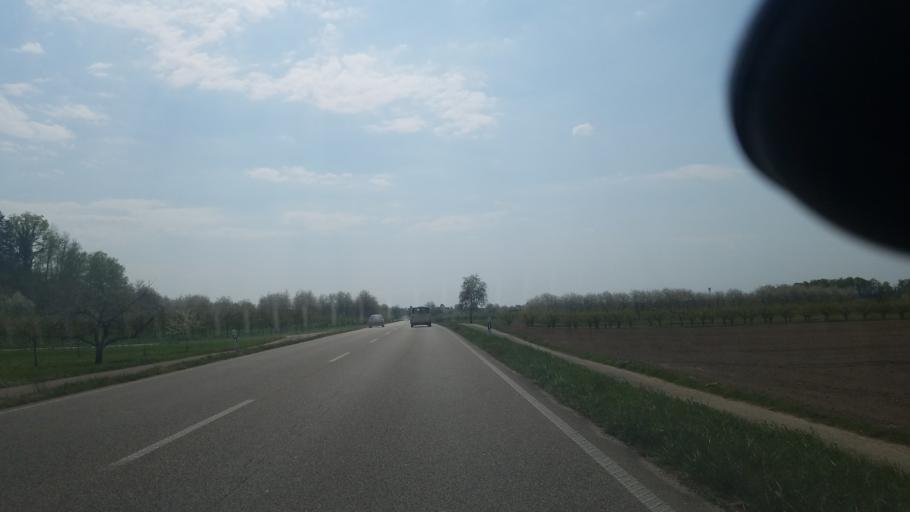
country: DE
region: Baden-Wuerttemberg
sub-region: Freiburg Region
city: Achern
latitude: 48.6178
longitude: 8.0453
